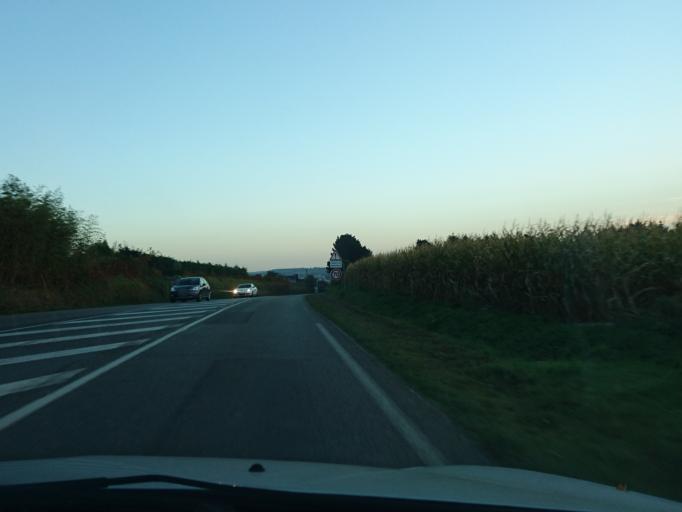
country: FR
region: Brittany
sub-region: Departement du Finistere
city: Saint-Renan
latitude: 48.4488
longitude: -4.6230
